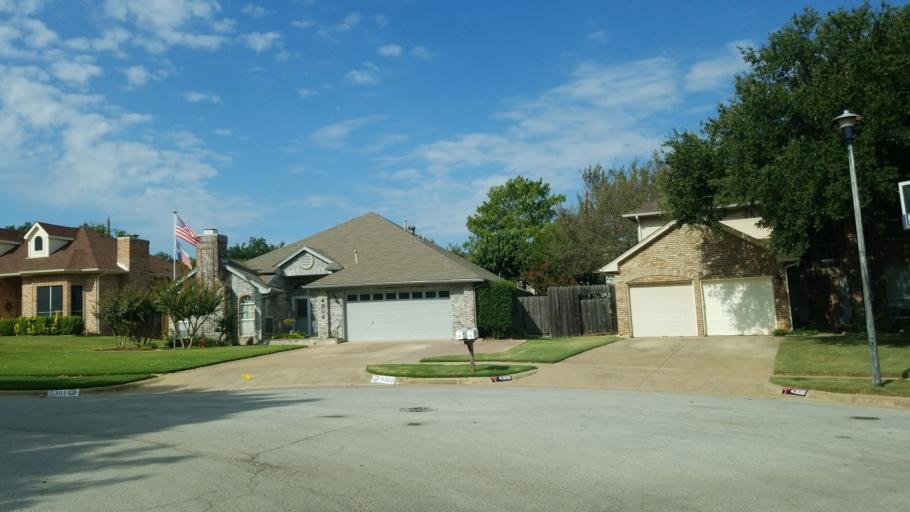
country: US
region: Texas
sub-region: Tarrant County
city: Grapevine
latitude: 32.8930
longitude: -97.0878
